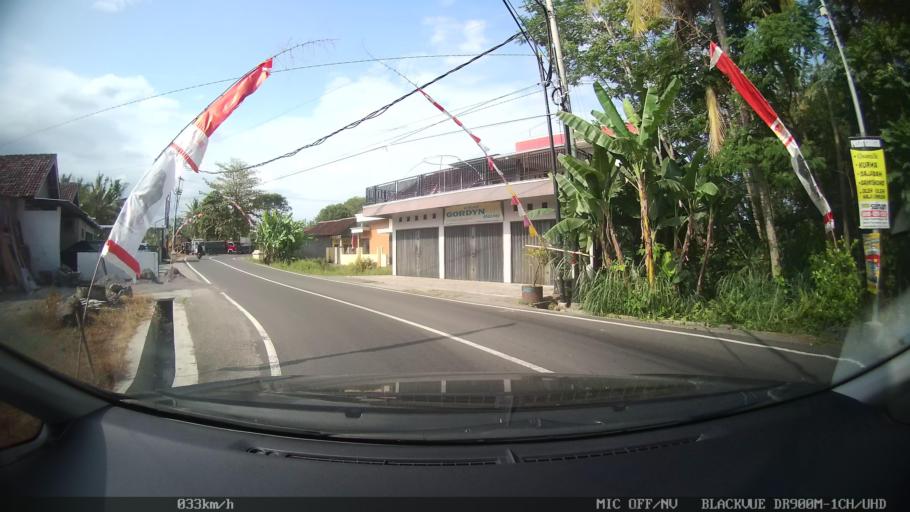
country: ID
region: Daerah Istimewa Yogyakarta
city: Depok
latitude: -7.7276
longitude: 110.4314
